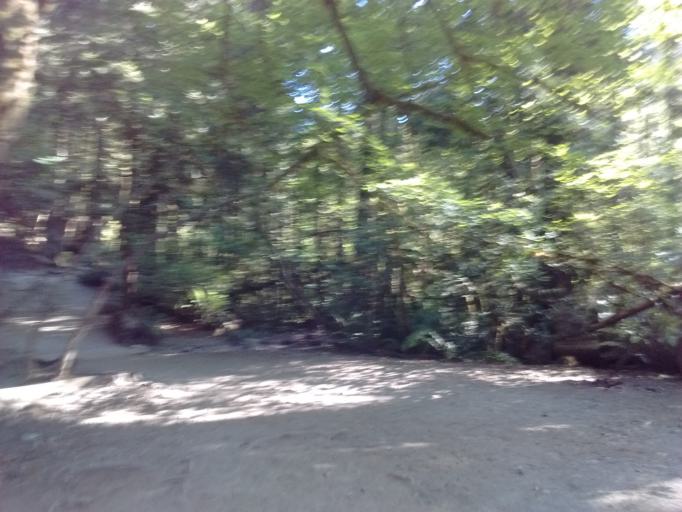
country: CA
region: British Columbia
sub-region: Fraser Valley Regional District
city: North Vancouver
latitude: 49.3461
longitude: -123.0196
